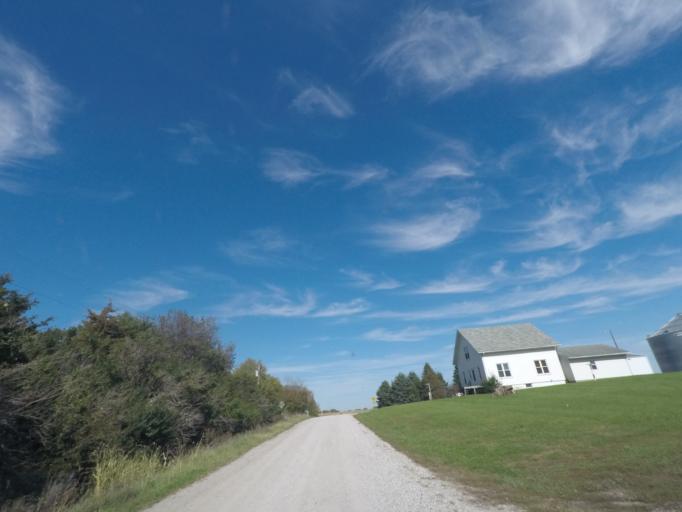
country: US
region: Iowa
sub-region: Story County
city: Nevada
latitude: 42.0101
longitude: -93.3476
